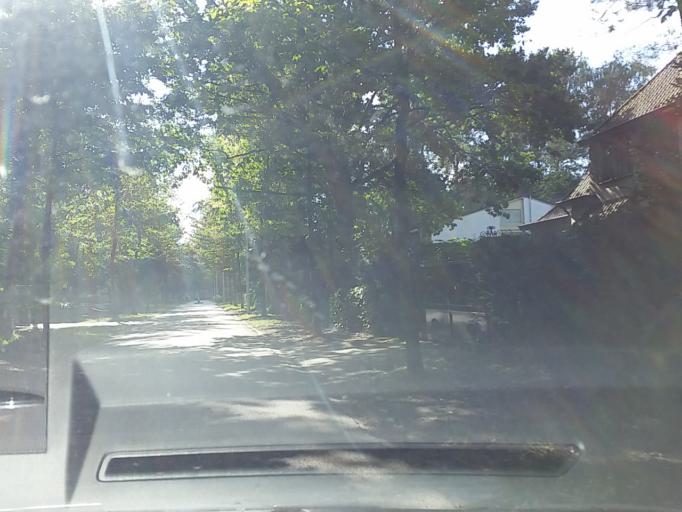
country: BE
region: Flanders
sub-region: Provincie Antwerpen
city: Schoten
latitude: 51.2635
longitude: 4.5206
